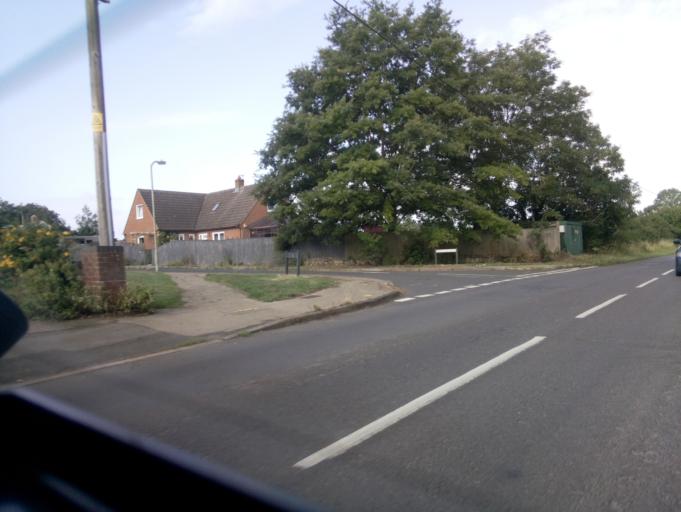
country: GB
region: England
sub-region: Oxfordshire
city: Faringdon
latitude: 51.6526
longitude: -1.5959
